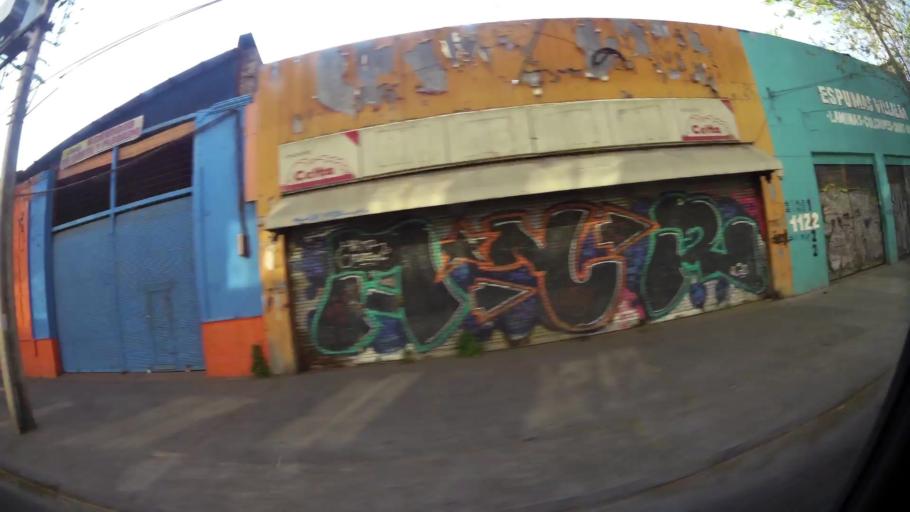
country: CL
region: Santiago Metropolitan
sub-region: Provincia de Santiago
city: Santiago
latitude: -33.4596
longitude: -70.6473
